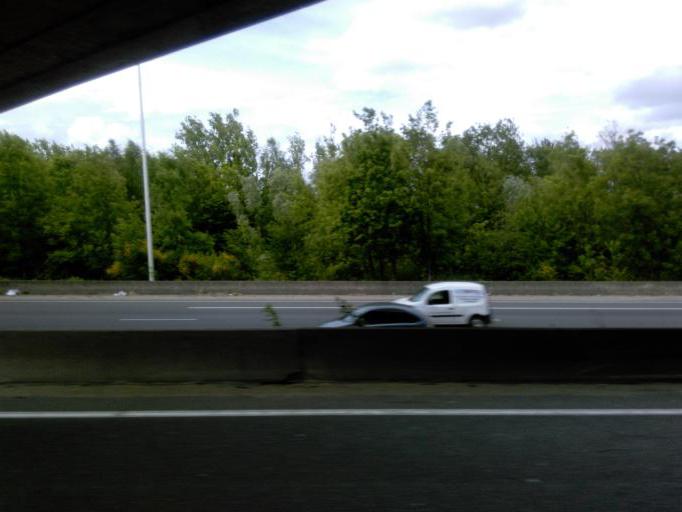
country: FR
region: Ile-de-France
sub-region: Departement du Val-d'Oise
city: Franconville
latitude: 48.9755
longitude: 2.2407
